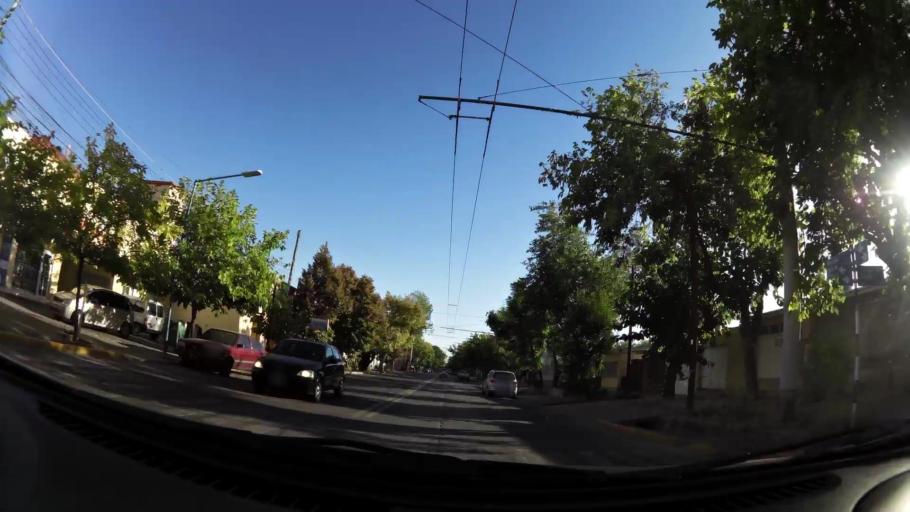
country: AR
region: Mendoza
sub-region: Departamento de Godoy Cruz
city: Godoy Cruz
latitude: -32.9434
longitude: -68.8486
